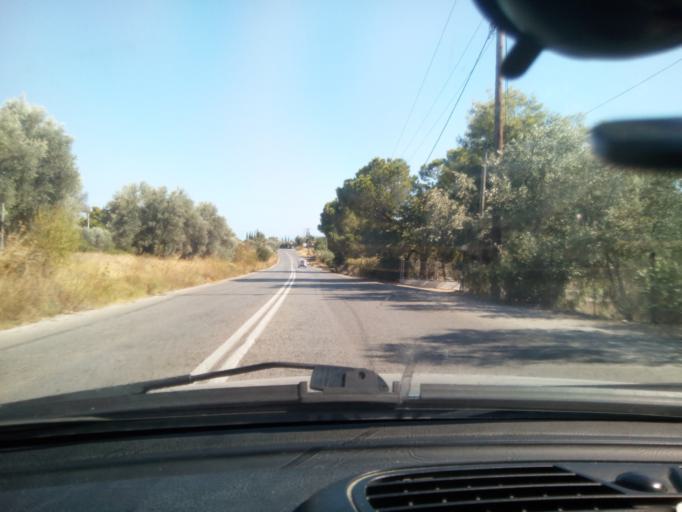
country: GR
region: Central Greece
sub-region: Nomos Evvoias
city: Filla
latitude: 38.4129
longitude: 23.7143
